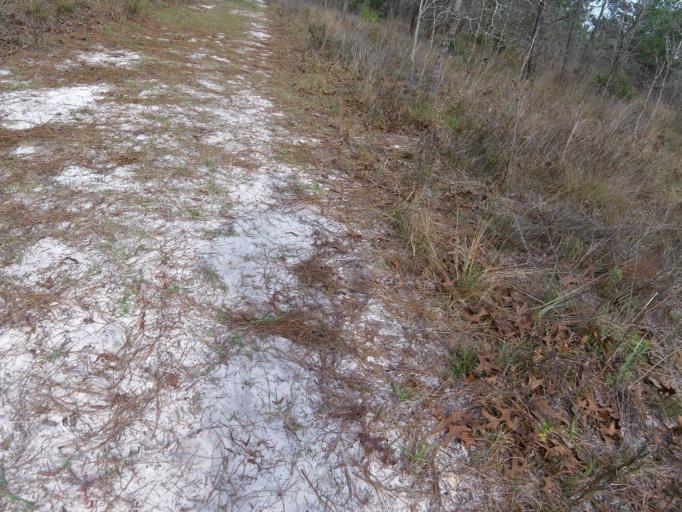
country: US
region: Florida
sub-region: Clay County
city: Middleburg
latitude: 30.1196
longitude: -81.8947
